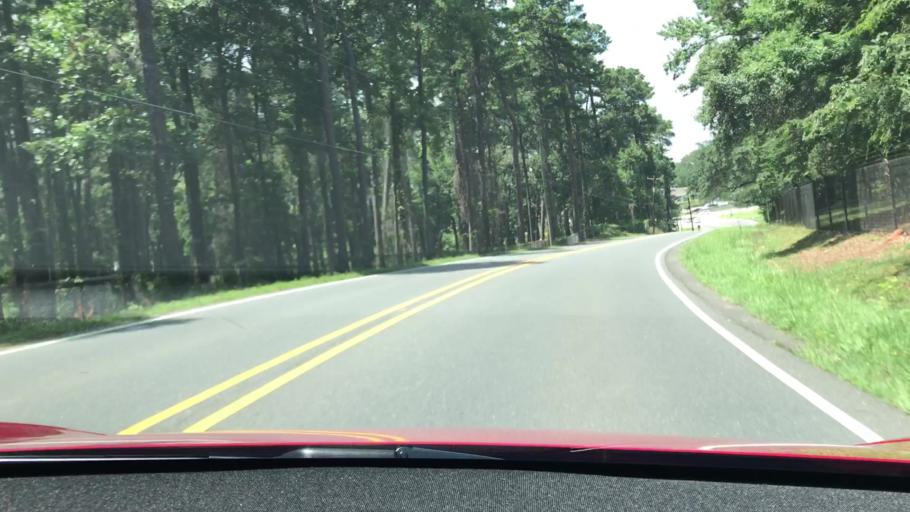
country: US
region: Louisiana
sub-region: Bossier Parish
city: Bossier City
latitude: 32.3917
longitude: -93.7240
